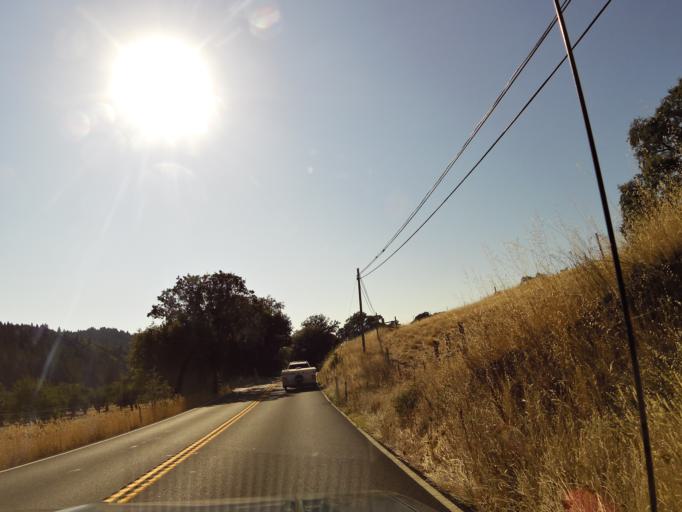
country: US
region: California
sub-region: Sonoma County
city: Cloverdale
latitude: 38.8855
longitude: -123.1477
